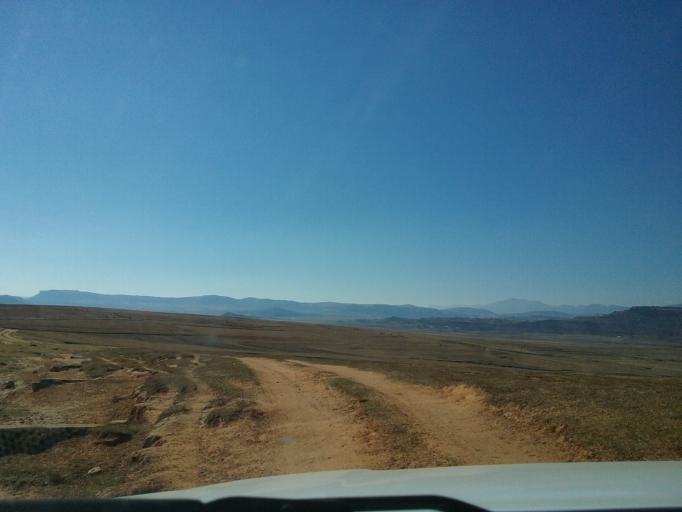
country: LS
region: Maseru
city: Nako
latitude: -29.4984
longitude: 27.5976
